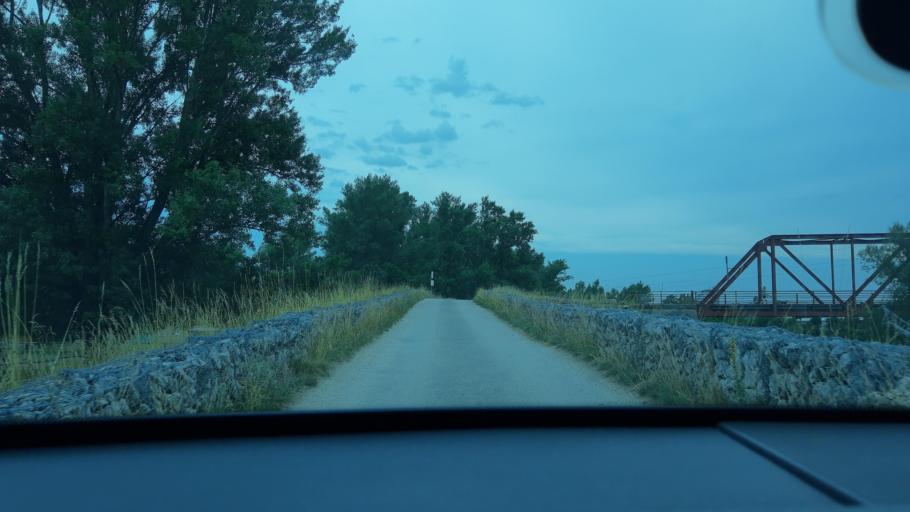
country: SK
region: Trnavsky
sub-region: Okres Trnava
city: Piestany
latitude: 48.6065
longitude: 17.8415
